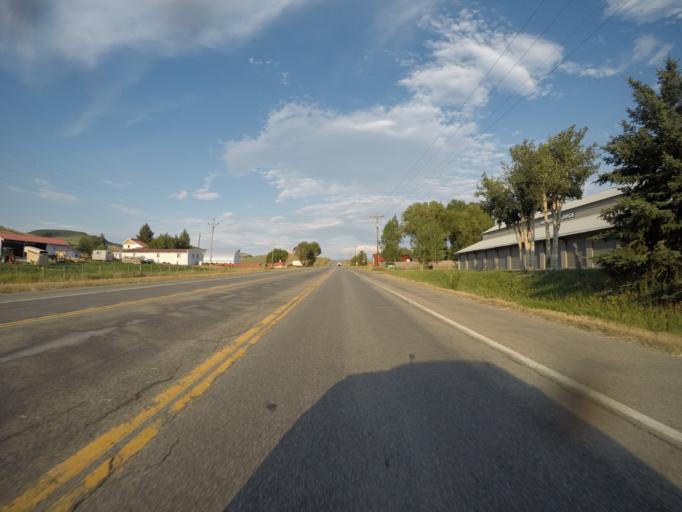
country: US
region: Colorado
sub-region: Routt County
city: Steamboat Springs
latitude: 40.4856
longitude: -107.0224
